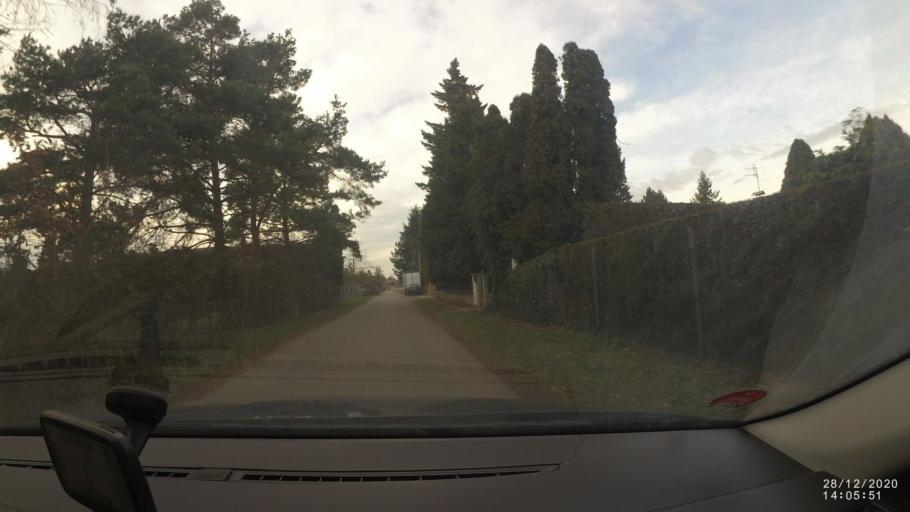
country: CZ
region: Central Bohemia
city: Sestajovice
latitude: 50.1003
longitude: 14.6660
